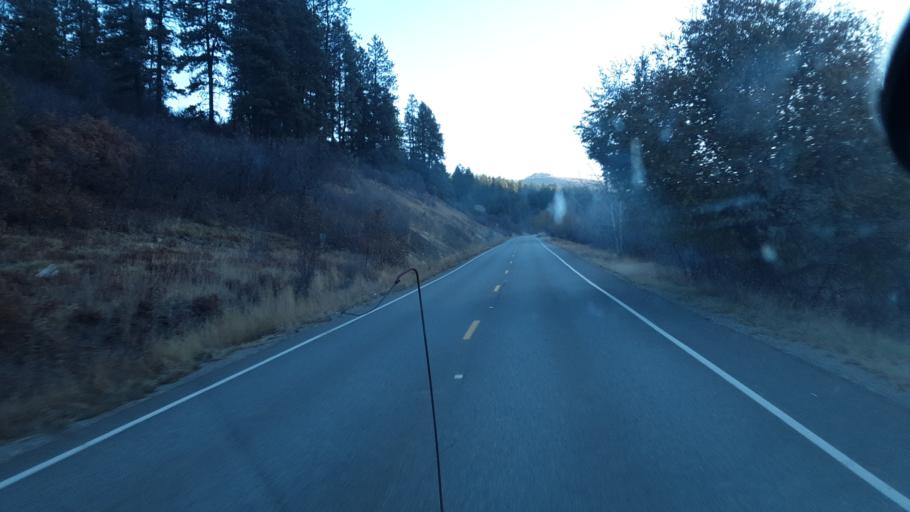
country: US
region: Colorado
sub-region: La Plata County
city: Bayfield
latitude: 37.3511
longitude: -107.6935
